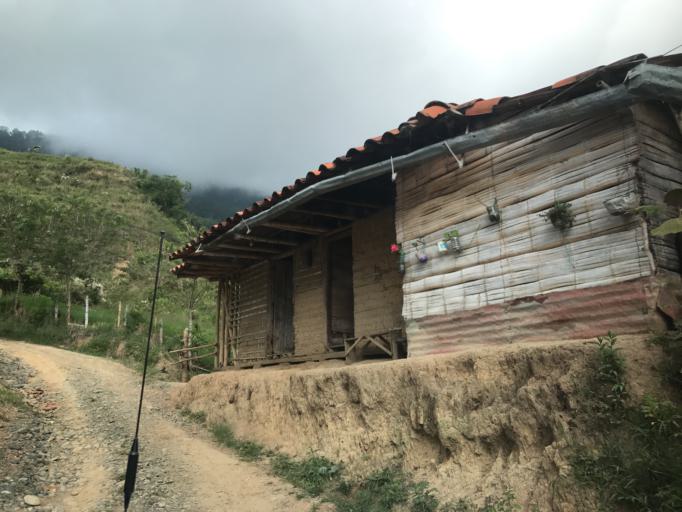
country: CO
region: Valle del Cauca
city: Obando
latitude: 4.5797
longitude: -75.8801
